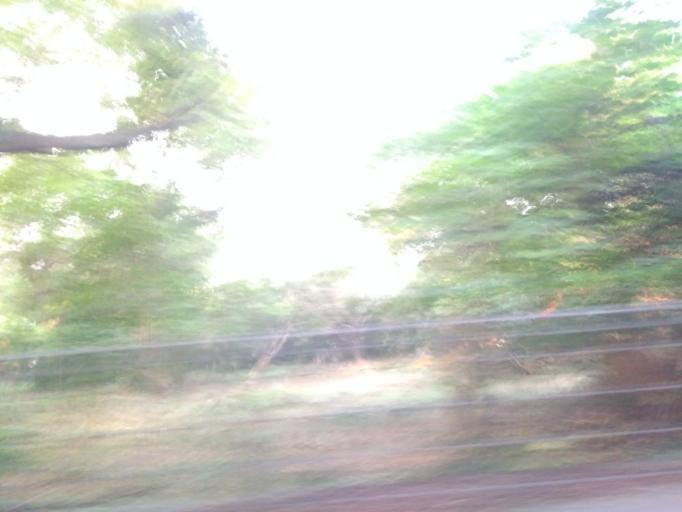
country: MY
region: Kuala Lumpur
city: Kuala Lumpur
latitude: 3.1338
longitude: 101.7043
